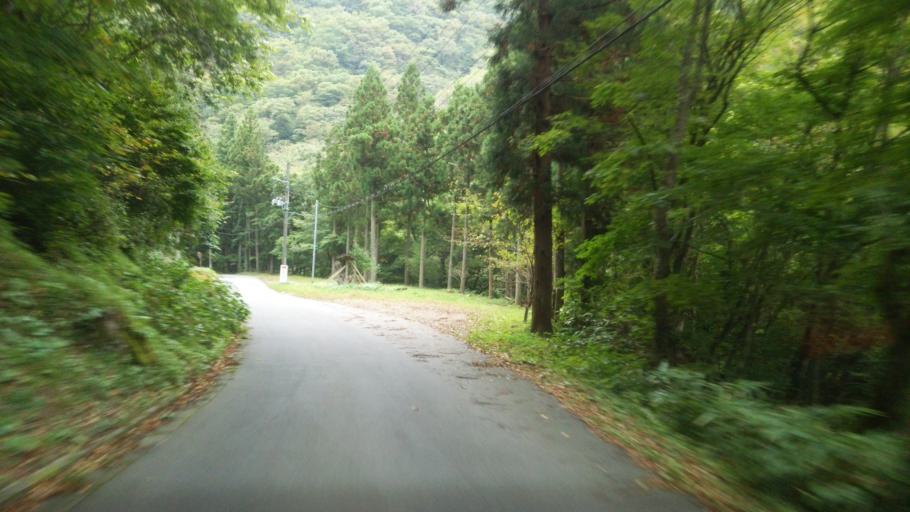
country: JP
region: Fukushima
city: Inawashiro
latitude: 37.3773
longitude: 139.9501
